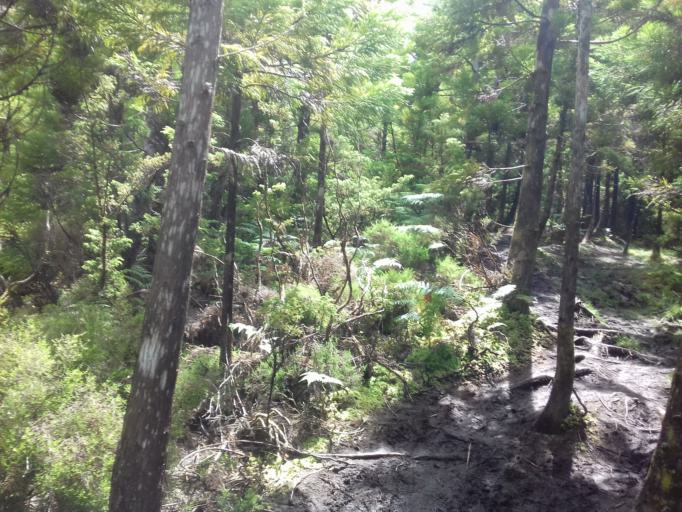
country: PT
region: Azores
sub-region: Praia da Vitoria
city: Biscoitos
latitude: 38.7307
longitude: -27.2823
